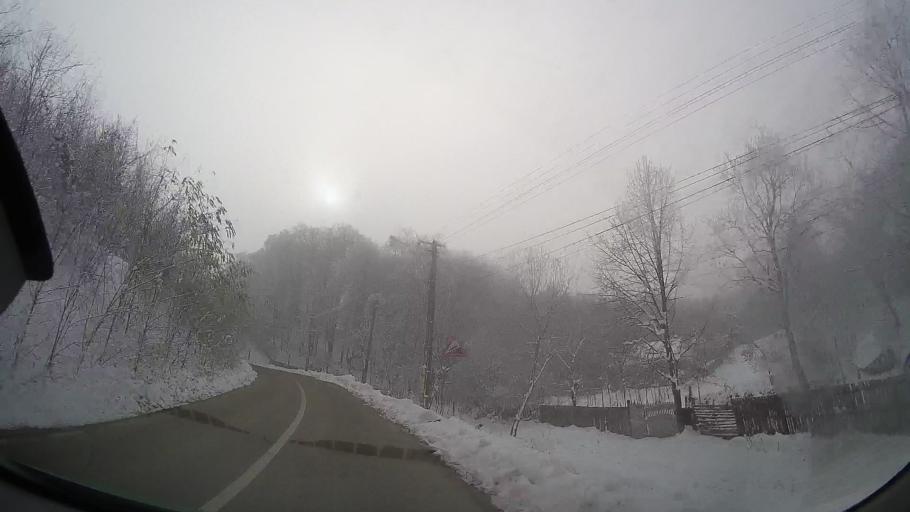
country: RO
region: Iasi
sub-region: Comuna Valea Seaca
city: Valea Seaca
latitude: 47.2861
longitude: 26.6684
